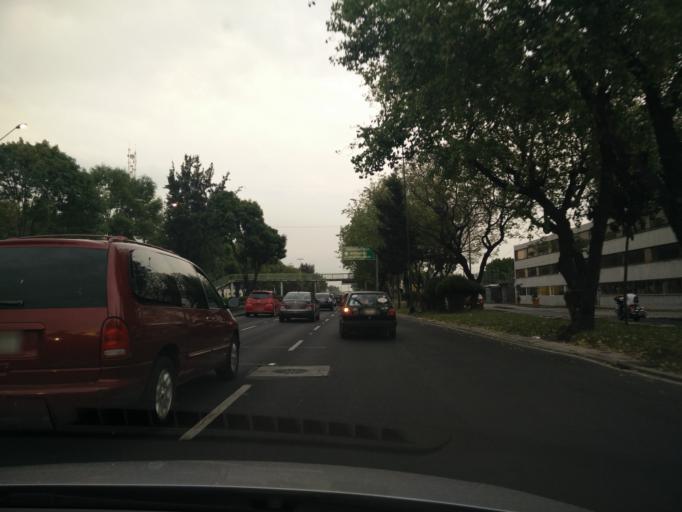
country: MX
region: Mexico City
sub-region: Iztacalco
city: Iztacalco
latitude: 19.4063
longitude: -99.1111
